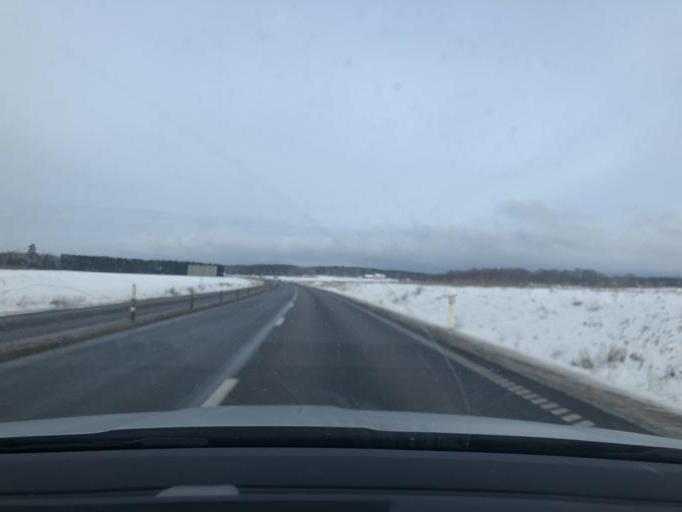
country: SE
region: OEstergoetland
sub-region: Motala Kommun
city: Borensberg
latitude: 58.5761
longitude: 15.2358
